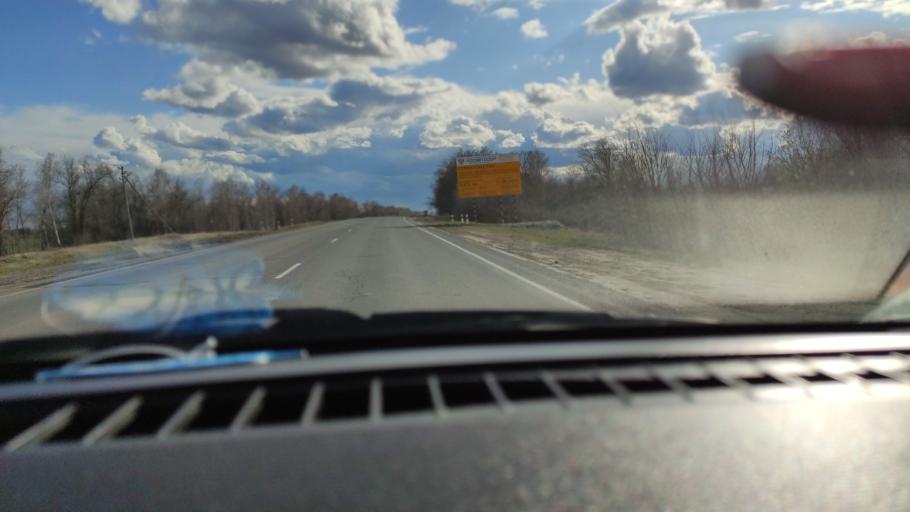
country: RU
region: Saratov
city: Sinodskoye
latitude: 52.0245
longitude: 46.7124
